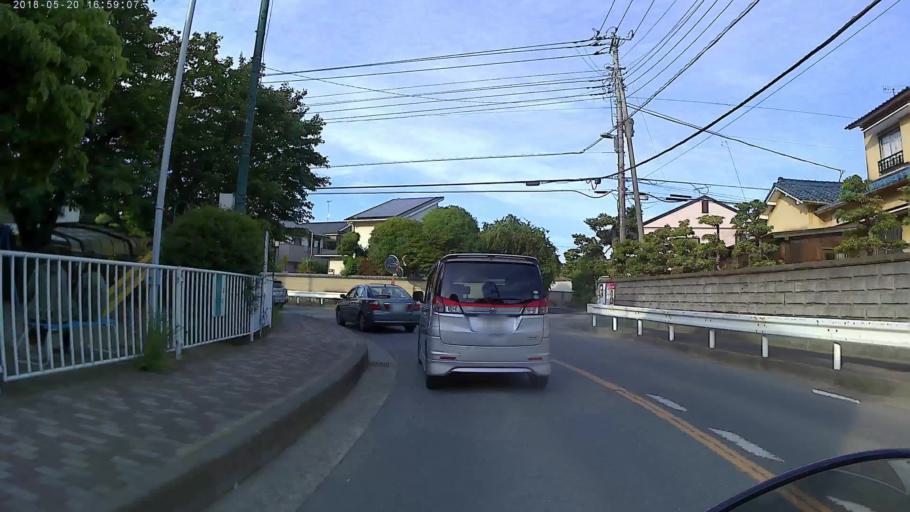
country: JP
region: Kanagawa
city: Odawara
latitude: 35.2850
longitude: 139.1797
